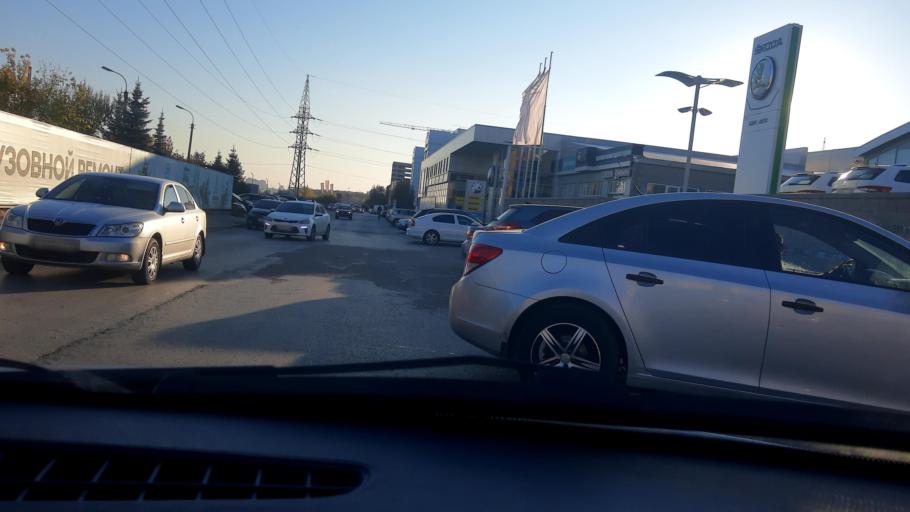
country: RU
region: Bashkortostan
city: Ufa
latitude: 54.7542
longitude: 56.0205
